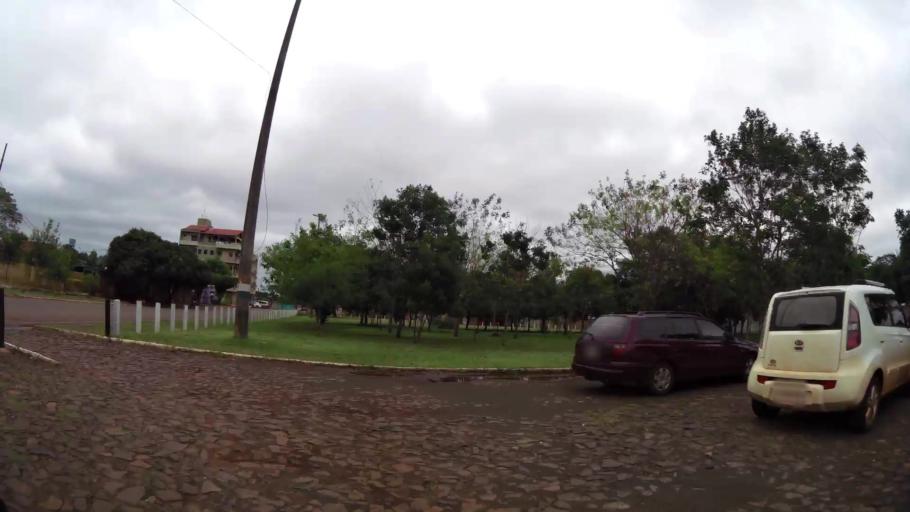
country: PY
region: Alto Parana
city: Ciudad del Este
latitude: -25.4853
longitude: -54.7646
